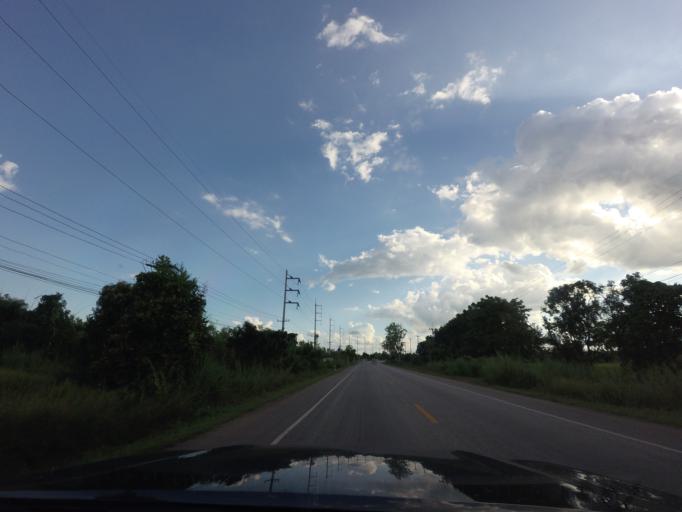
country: TH
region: Changwat Udon Thani
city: Thung Fon
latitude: 17.4708
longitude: 103.1934
